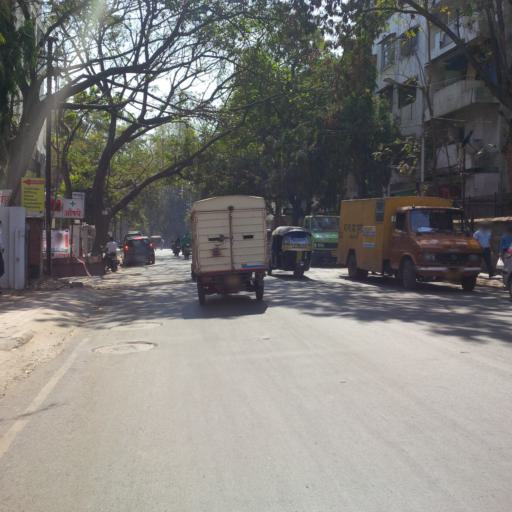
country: IN
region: Maharashtra
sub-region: Pune Division
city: Pune
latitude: 18.5147
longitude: 73.8288
